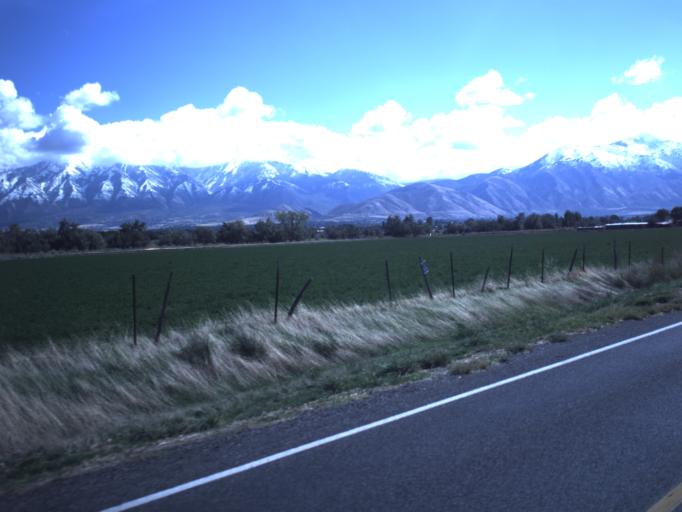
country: US
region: Utah
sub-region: Utah County
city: West Mountain
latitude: 40.0851
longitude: -111.7880
